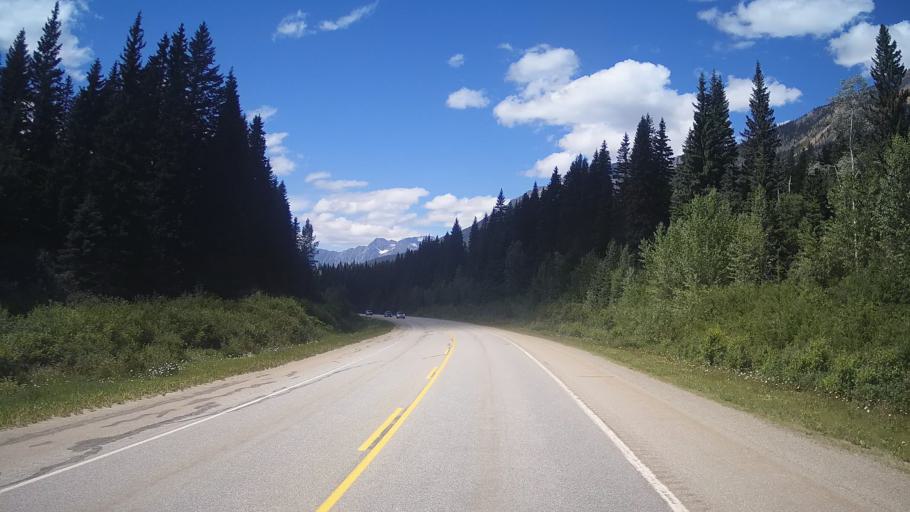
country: CA
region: Alberta
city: Grande Cache
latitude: 53.0001
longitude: -119.0305
